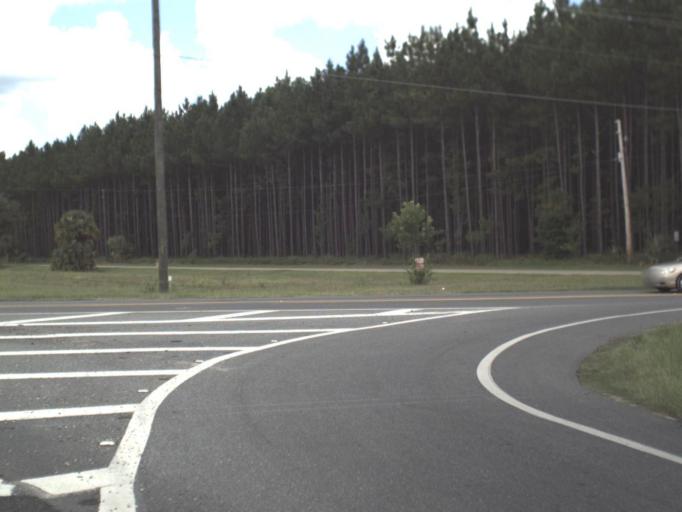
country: US
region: Florida
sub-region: Taylor County
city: Perry
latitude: 30.1277
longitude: -83.5969
